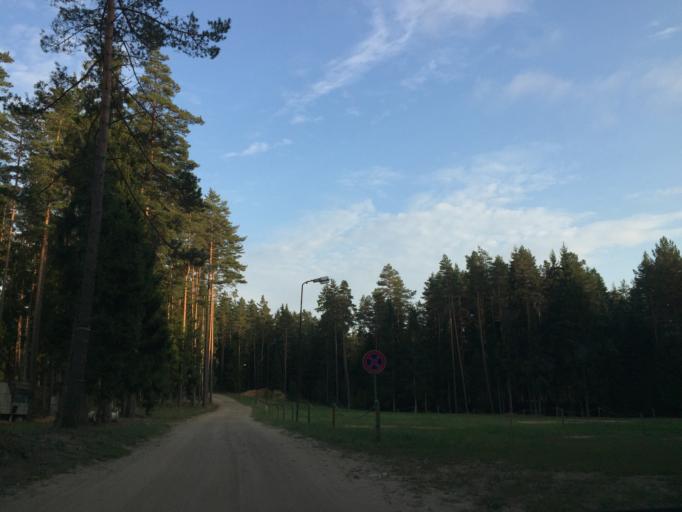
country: LV
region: Baldone
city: Baldone
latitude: 56.7704
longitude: 24.3996
